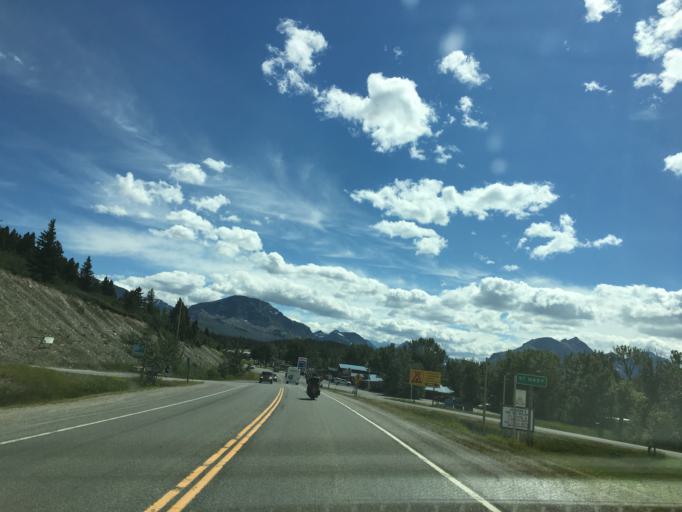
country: US
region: Montana
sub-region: Glacier County
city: North Browning
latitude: 48.7483
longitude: -113.4281
